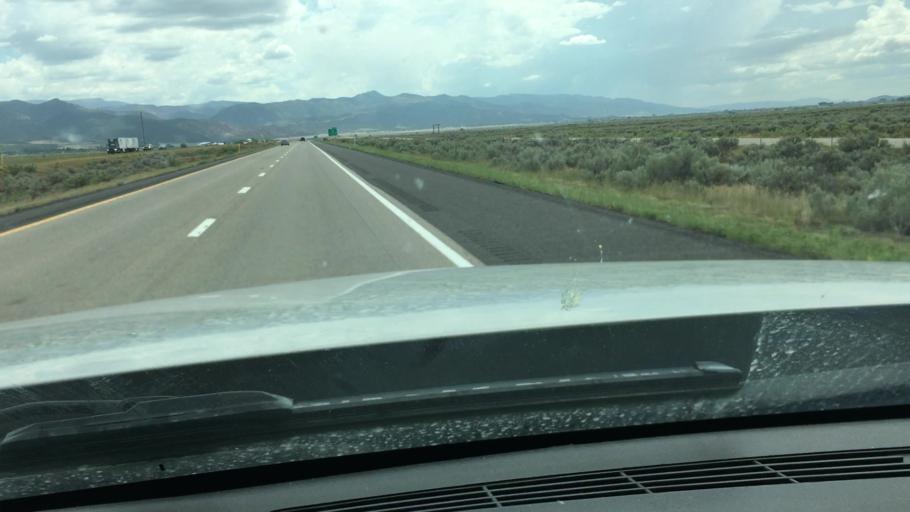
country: US
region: Utah
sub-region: Iron County
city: Parowan
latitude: 37.9284
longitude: -112.7664
